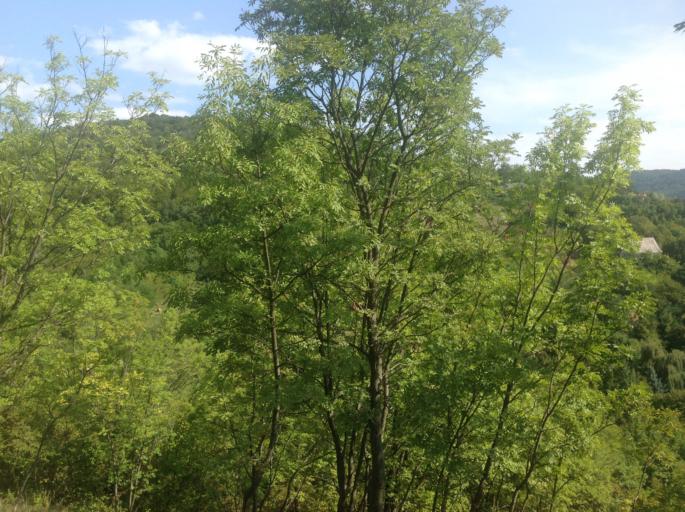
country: HU
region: Pest
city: Visegrad
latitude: 47.7903
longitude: 18.9764
